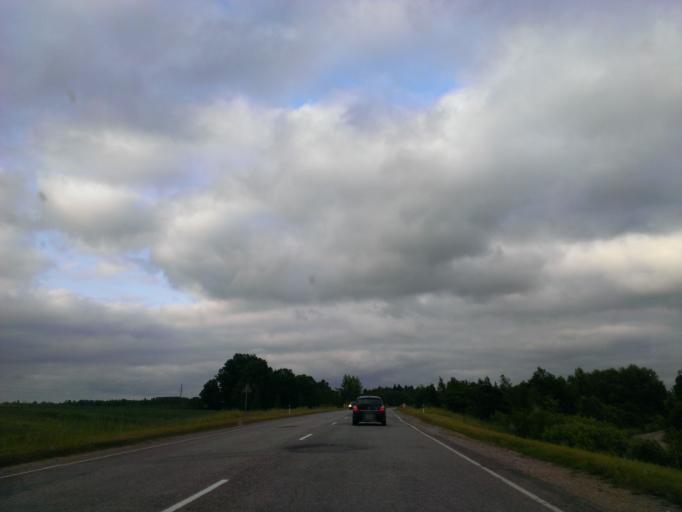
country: LV
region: Saldus Rajons
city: Saldus
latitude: 56.6721
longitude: 22.3741
